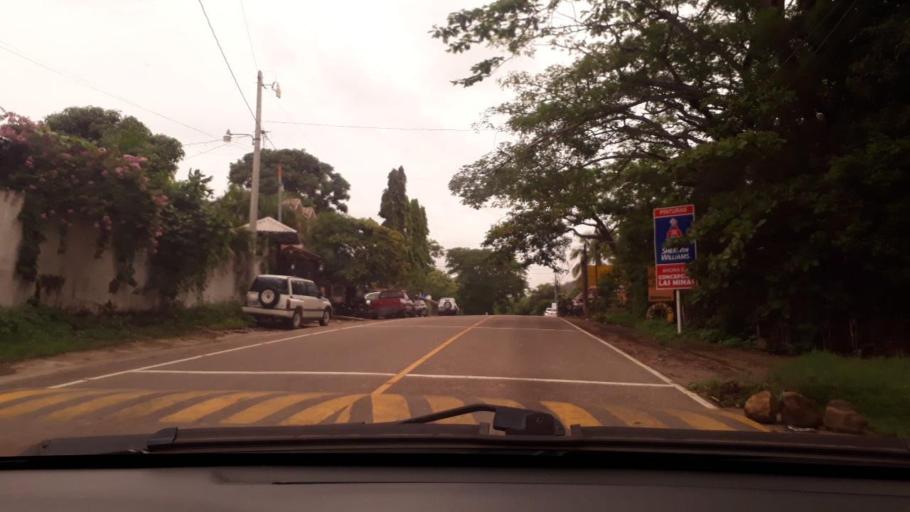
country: GT
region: Chiquimula
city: Concepcion Las Minas
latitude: 14.5152
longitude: -89.4686
